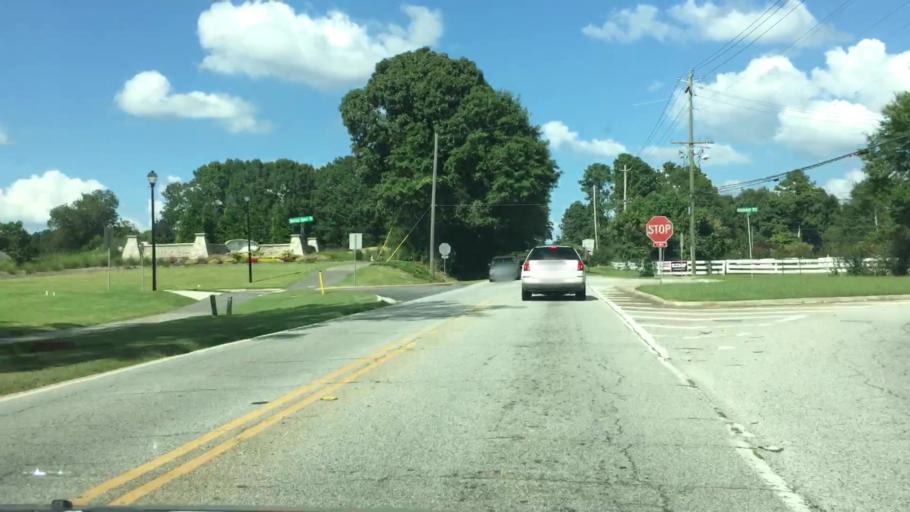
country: US
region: Georgia
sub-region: Fayette County
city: Fayetteville
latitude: 33.4293
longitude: -84.4616
